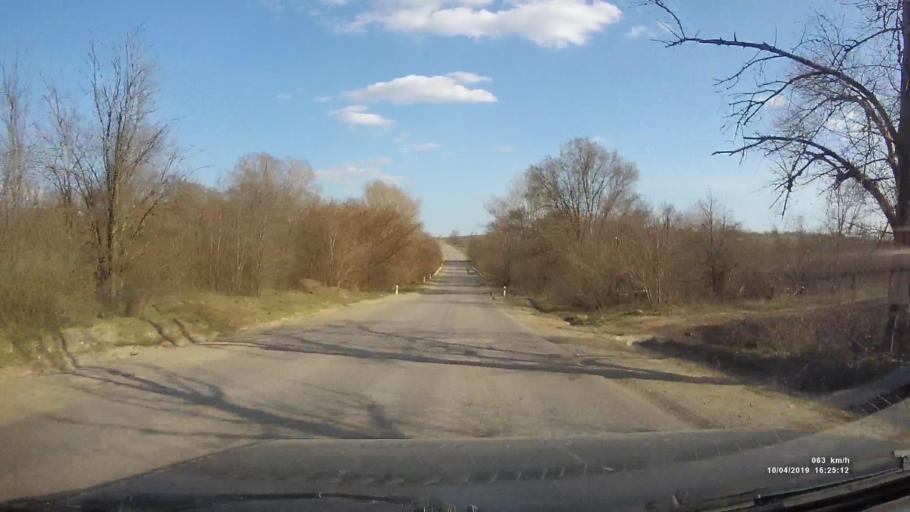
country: RU
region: Rostov
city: Staraya Stanitsa
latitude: 48.2943
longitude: 40.3214
